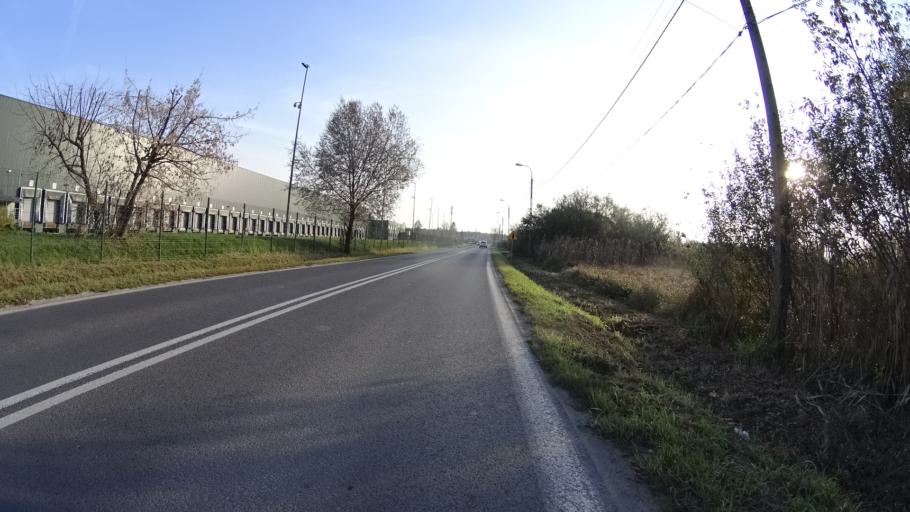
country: PL
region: Masovian Voivodeship
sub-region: Powiat warszawski zachodni
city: Babice
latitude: 52.2846
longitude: 20.8672
